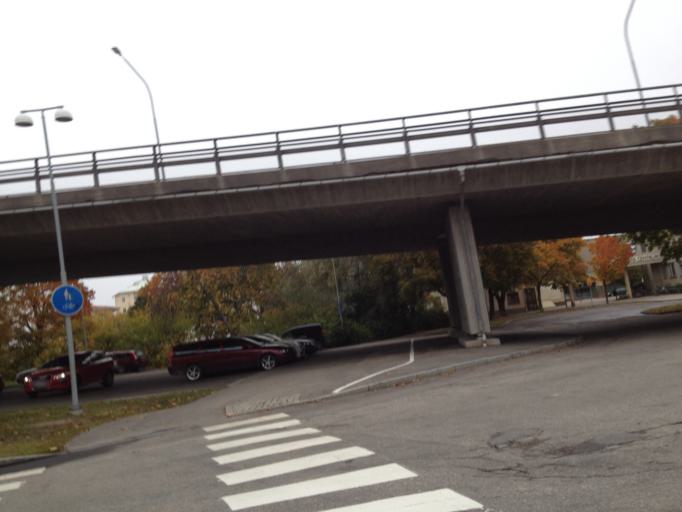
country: SE
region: Gaevleborg
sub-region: Bollnas Kommun
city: Bollnas
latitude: 61.3464
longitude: 16.3912
